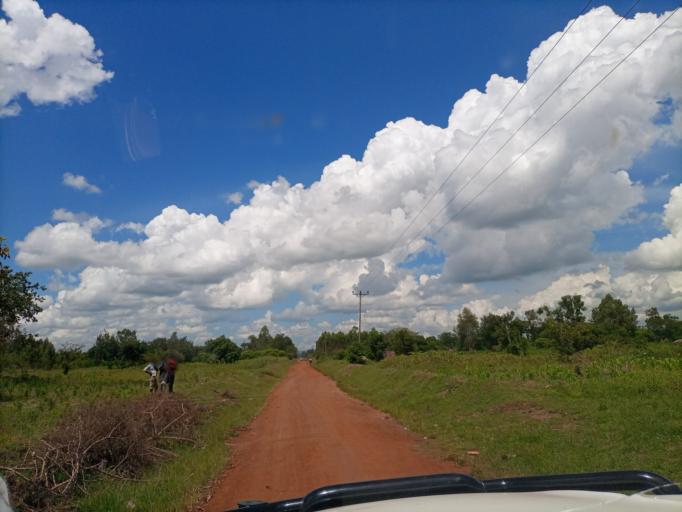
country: UG
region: Eastern Region
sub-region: Tororo District
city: Tororo
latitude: 0.6684
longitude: 34.0031
